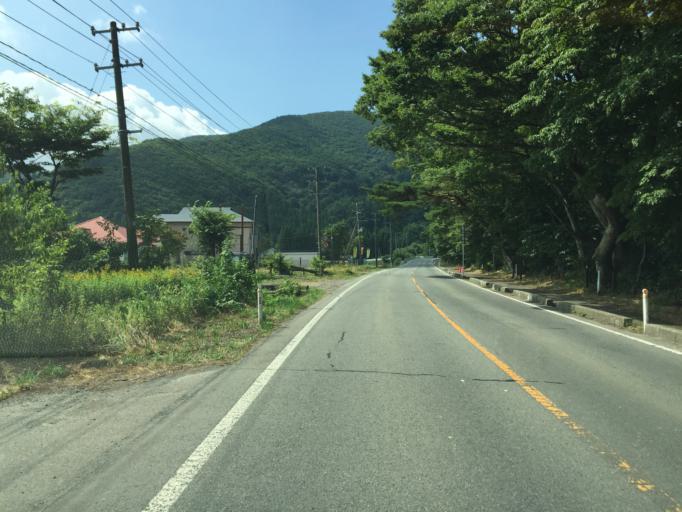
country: JP
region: Fukushima
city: Inawashiro
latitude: 37.4876
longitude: 140.1552
